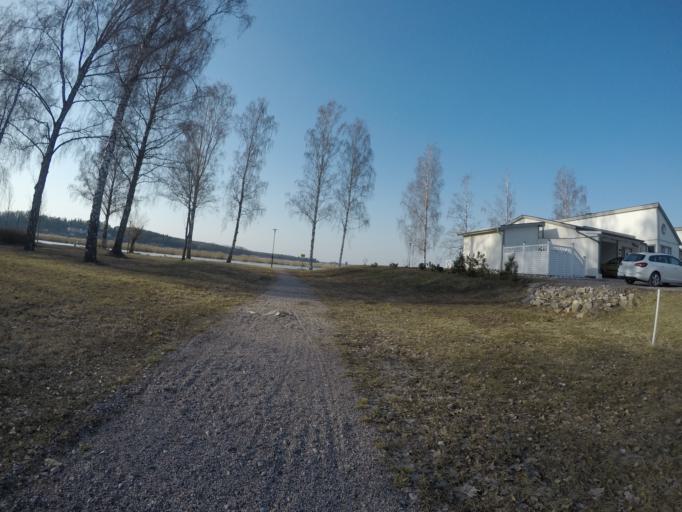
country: SE
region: Vaestmanland
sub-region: Kungsors Kommun
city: Kungsoer
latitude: 59.4284
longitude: 16.1017
